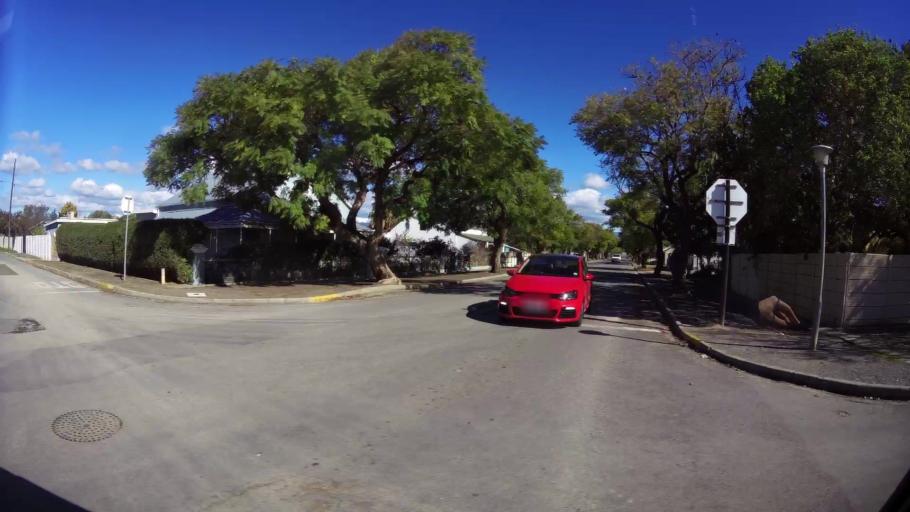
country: ZA
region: Western Cape
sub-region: Cape Winelands District Municipality
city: Ashton
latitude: -33.7981
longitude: 19.8887
